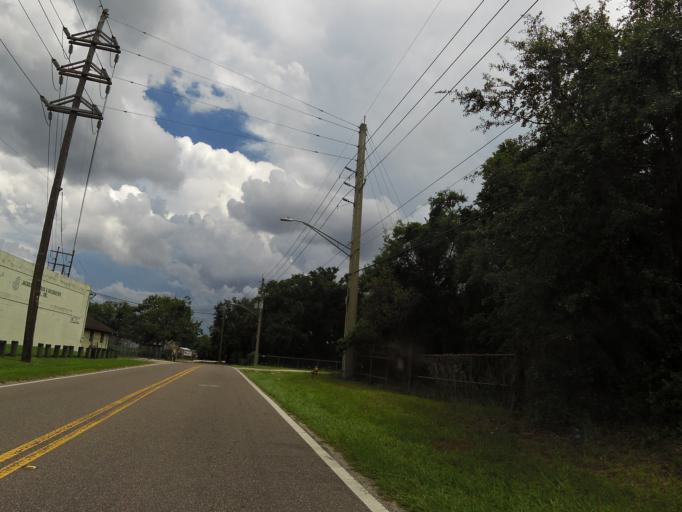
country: US
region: Florida
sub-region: Duval County
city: Jacksonville
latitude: 30.3698
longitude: -81.6391
